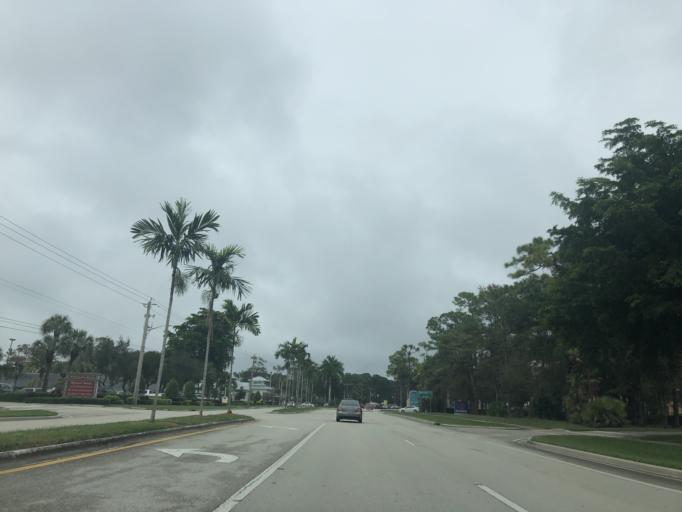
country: US
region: Florida
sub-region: Palm Beach County
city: Wellington
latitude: 26.6709
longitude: -80.2468
